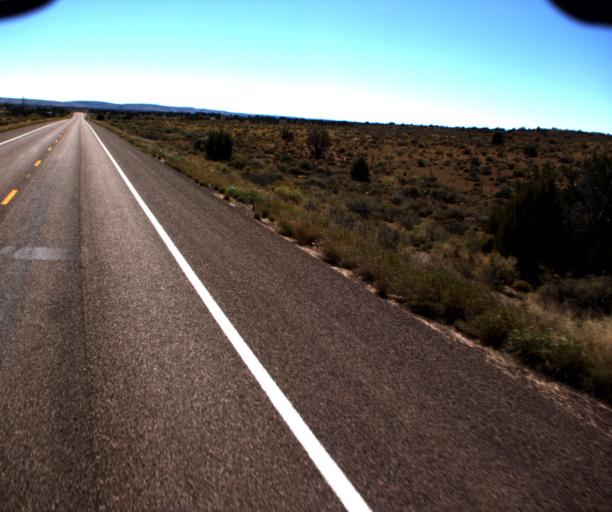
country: US
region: Arizona
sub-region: Apache County
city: Saint Johns
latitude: 34.6238
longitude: -109.6680
